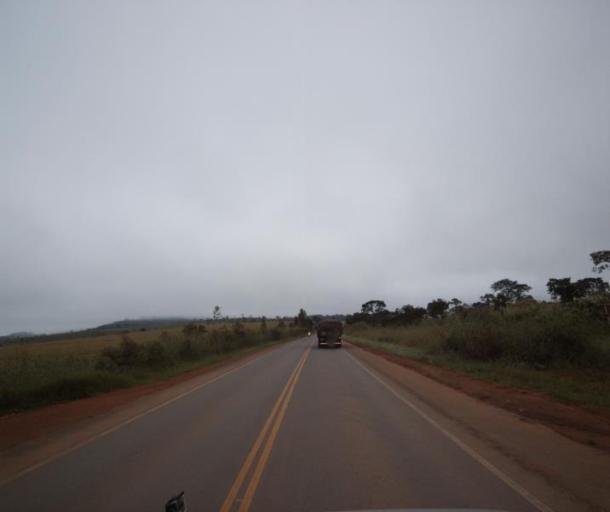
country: BR
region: Goias
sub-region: Pirenopolis
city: Pirenopolis
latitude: -15.9688
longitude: -48.8230
